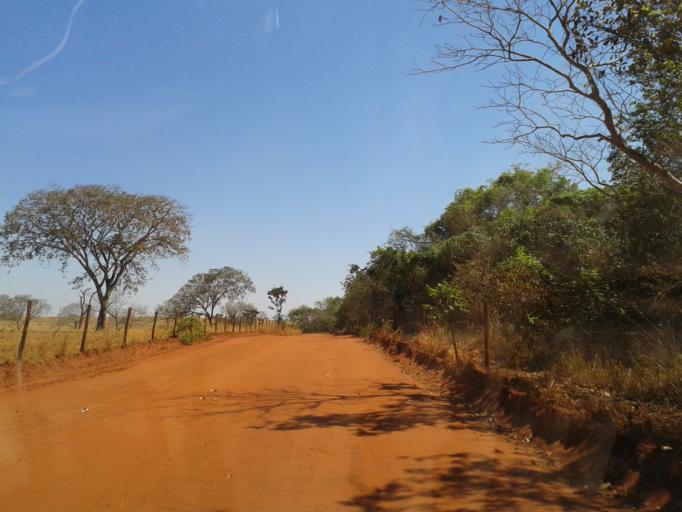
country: BR
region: Minas Gerais
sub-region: Ituiutaba
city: Ituiutaba
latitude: -18.9887
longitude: -49.3872
